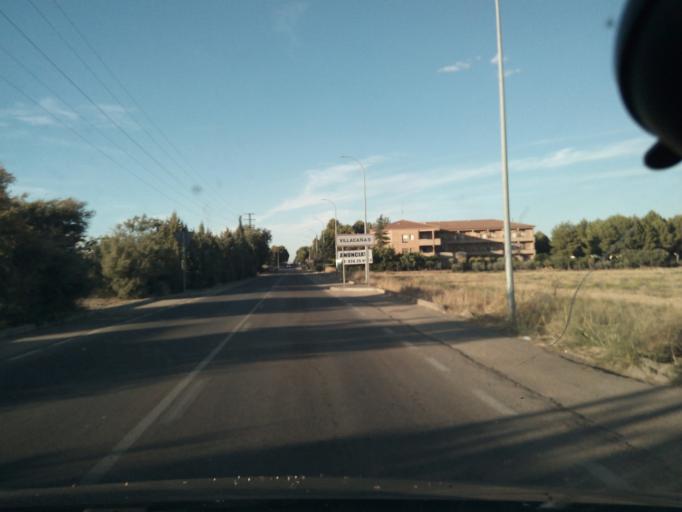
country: ES
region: Castille-La Mancha
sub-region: Province of Toledo
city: Villacanas
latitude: 39.6107
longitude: -3.3460
